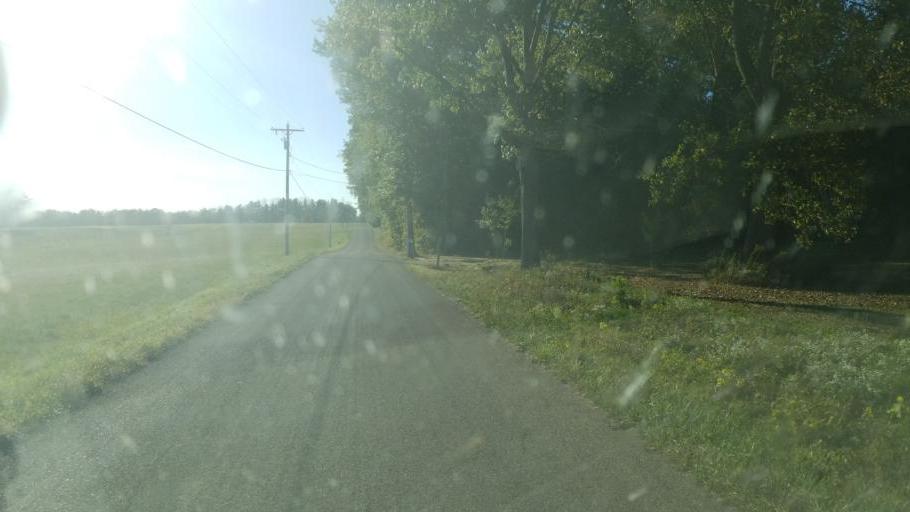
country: US
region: Ohio
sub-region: Richland County
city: Lexington
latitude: 40.6373
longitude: -82.6281
